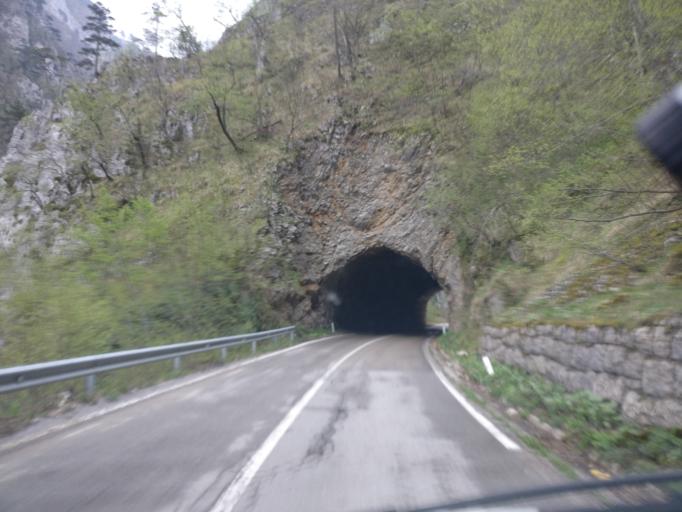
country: ME
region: Opstina Pluzine
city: Pluzine
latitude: 43.2889
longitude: 18.8498
